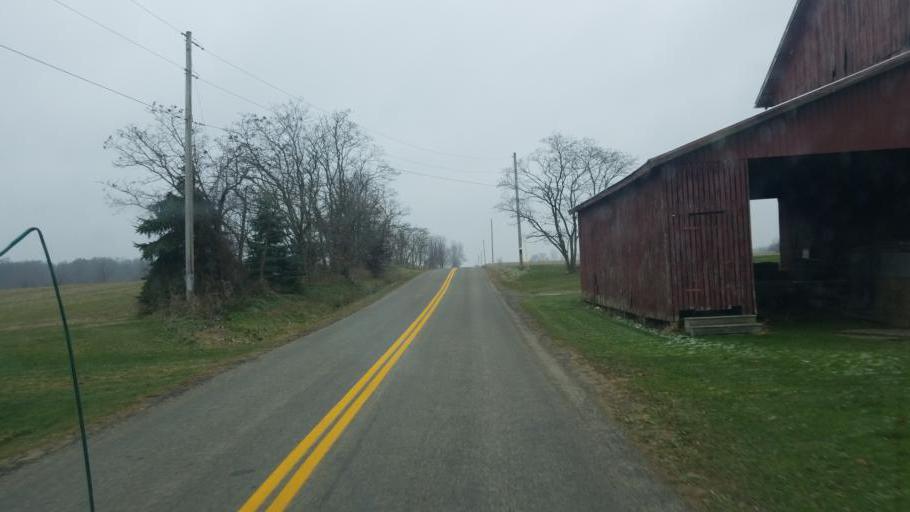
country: US
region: Ohio
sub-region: Huron County
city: New London
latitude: 40.9940
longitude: -82.3546
